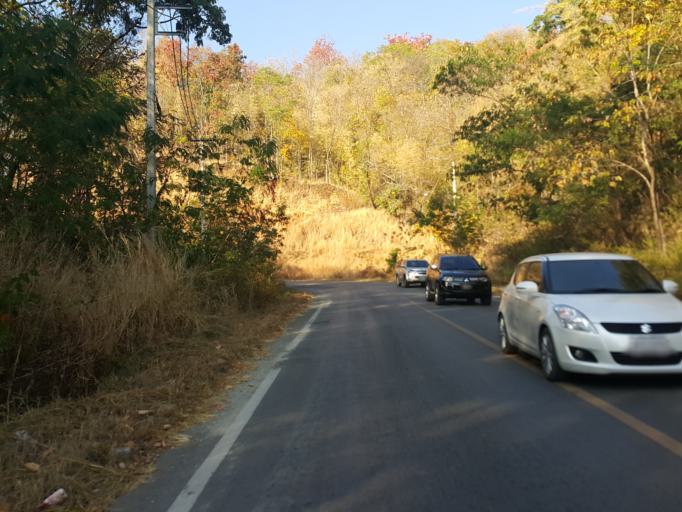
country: TH
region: Chiang Mai
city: Mae On
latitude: 18.8285
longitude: 99.2603
